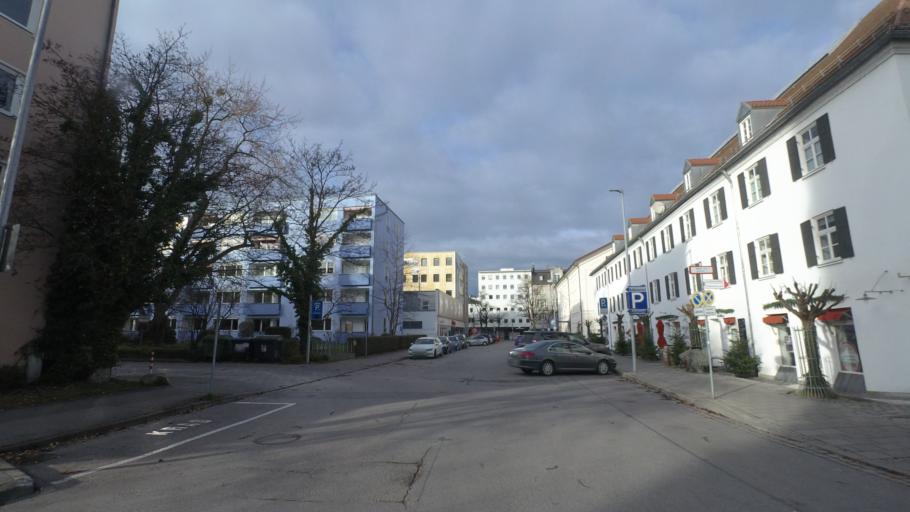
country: DE
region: Bavaria
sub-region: Upper Bavaria
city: Rosenheim
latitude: 47.8526
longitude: 12.1233
